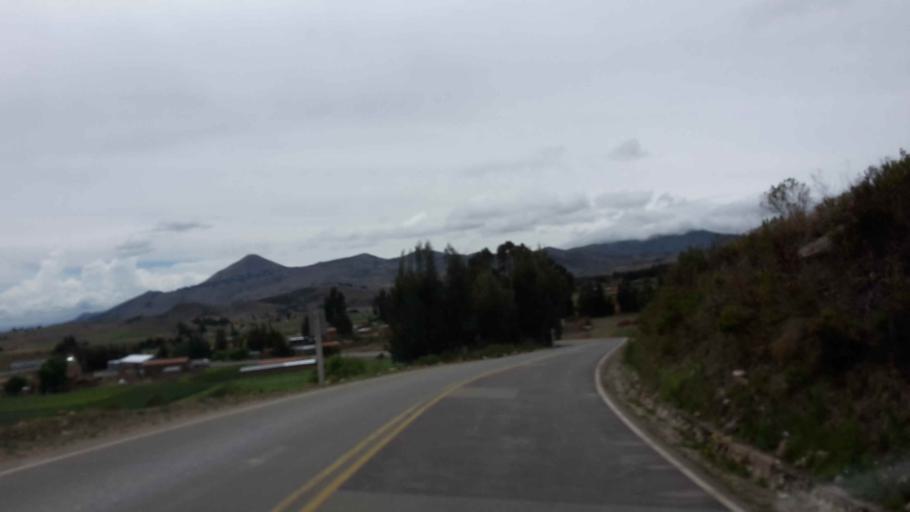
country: BO
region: Cochabamba
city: Arani
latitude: -17.4552
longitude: -65.7151
